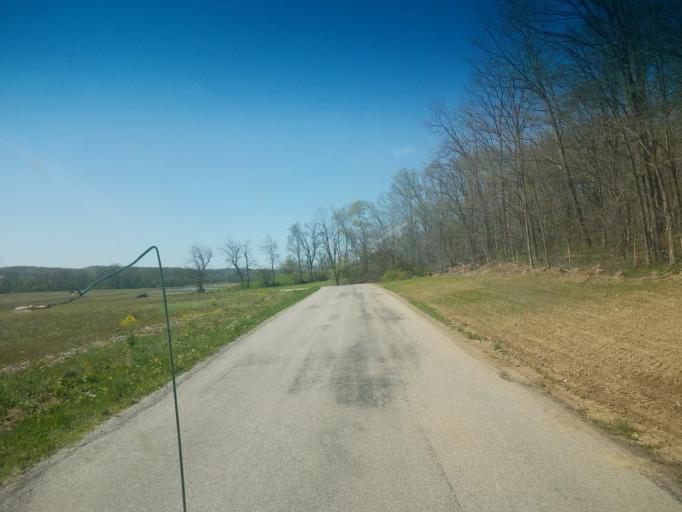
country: US
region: Ohio
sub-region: Medina County
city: Lodi
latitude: 40.9464
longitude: -82.0175
